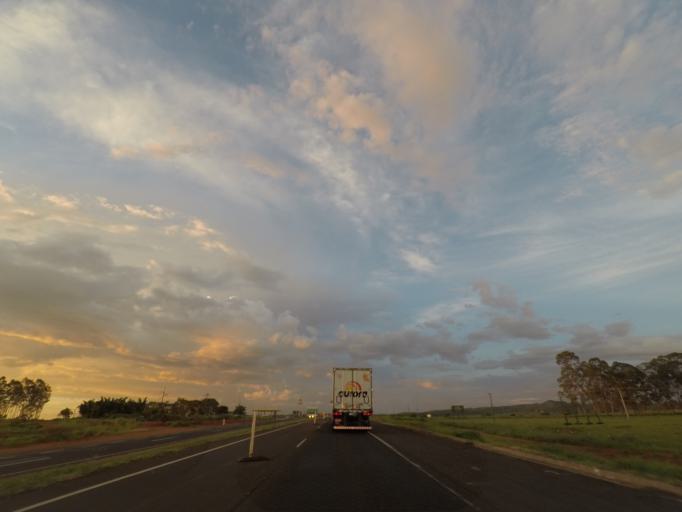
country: BR
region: Minas Gerais
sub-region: Uberaba
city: Uberaba
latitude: -19.6296
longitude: -48.0139
